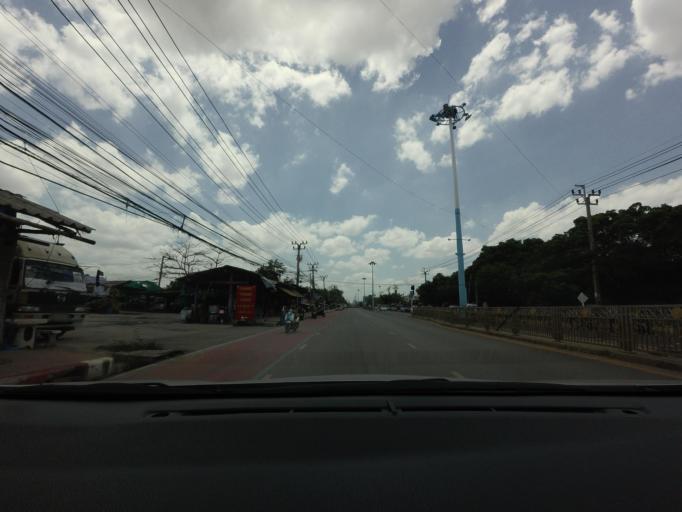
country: TH
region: Samut Prakan
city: Samut Prakan
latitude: 13.5650
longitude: 100.5906
